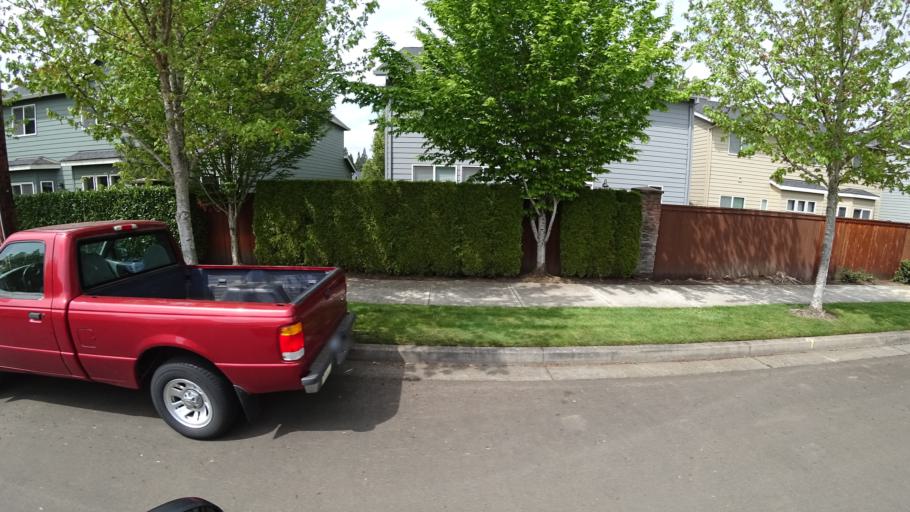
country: US
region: Oregon
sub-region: Washington County
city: Hillsboro
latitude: 45.5471
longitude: -122.9990
